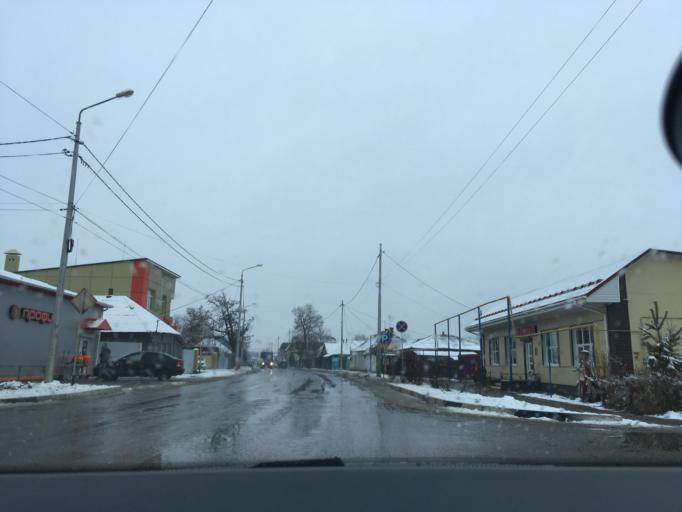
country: RU
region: Belgorod
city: Valuyki
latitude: 50.2025
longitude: 38.1129
